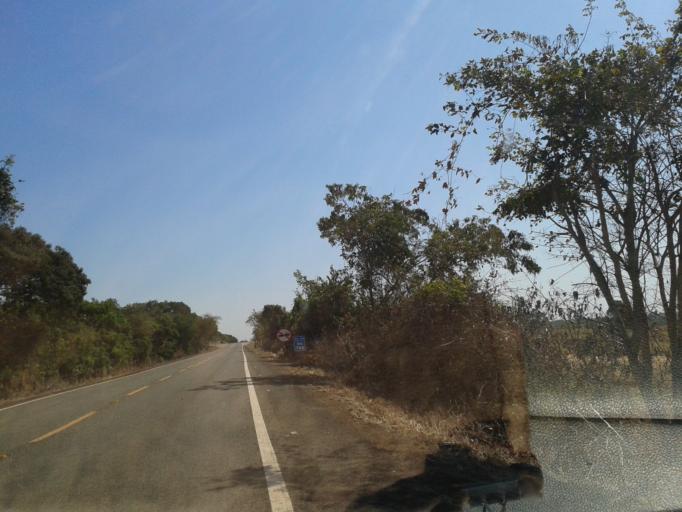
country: BR
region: Goias
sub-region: Sao Miguel Do Araguaia
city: Sao Miguel do Araguaia
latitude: -13.8939
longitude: -50.3278
